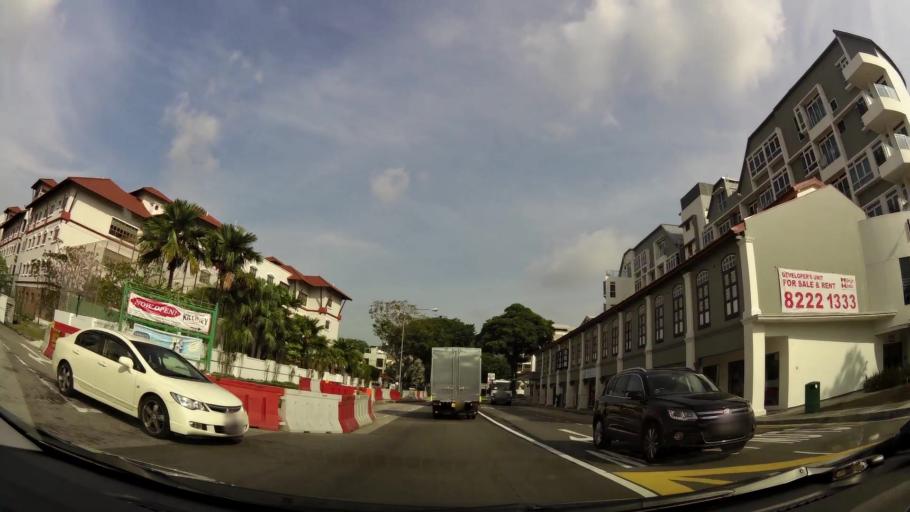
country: SG
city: Singapore
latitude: 1.2791
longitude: 103.7857
